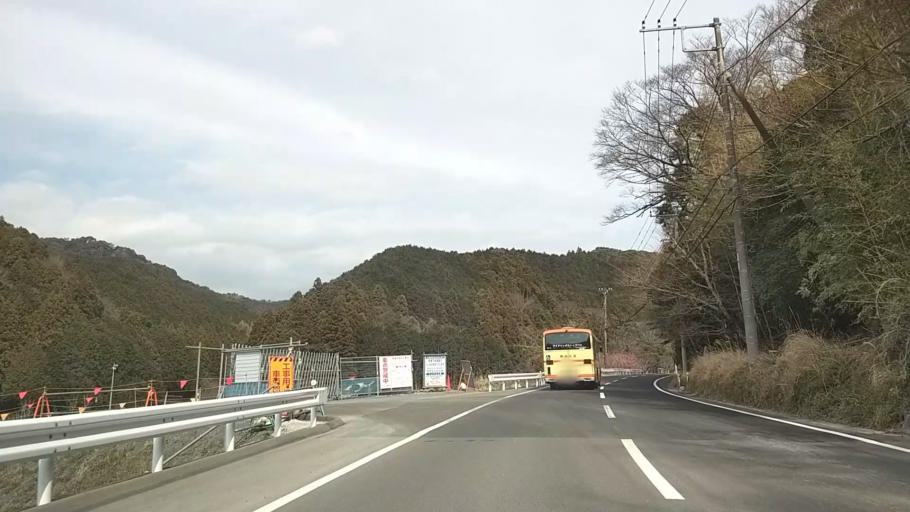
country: JP
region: Shizuoka
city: Shimoda
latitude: 34.7571
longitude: 138.9485
